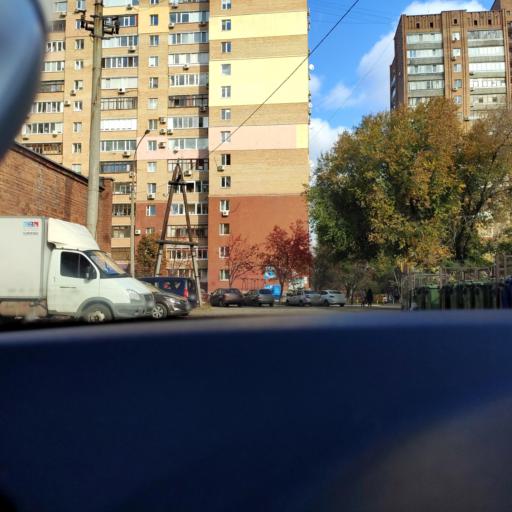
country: RU
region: Samara
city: Samara
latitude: 53.2587
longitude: 50.2394
